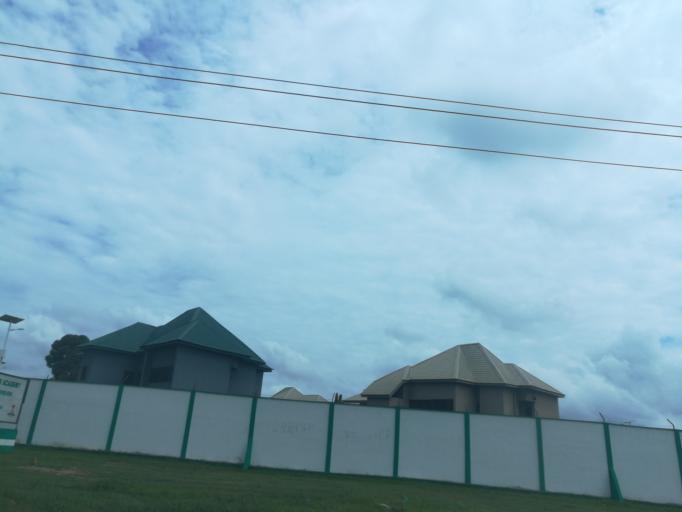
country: NG
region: Lagos
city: Ikotun
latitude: 6.4939
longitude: 3.1497
